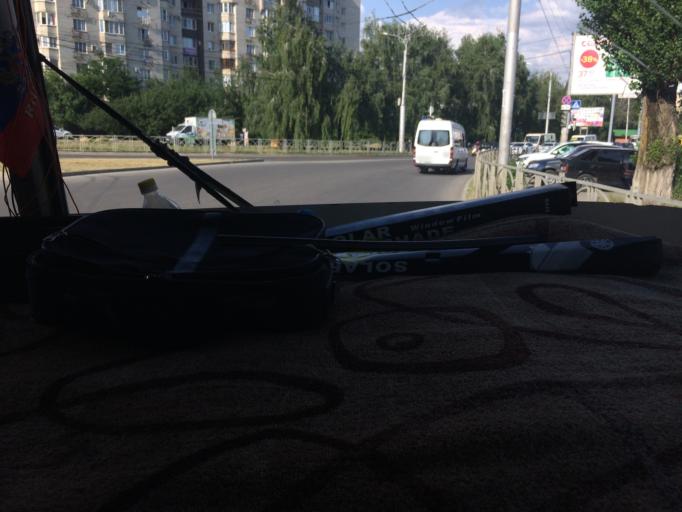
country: RU
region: Stavropol'skiy
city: Stavropol'
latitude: 45.0141
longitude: 41.9151
